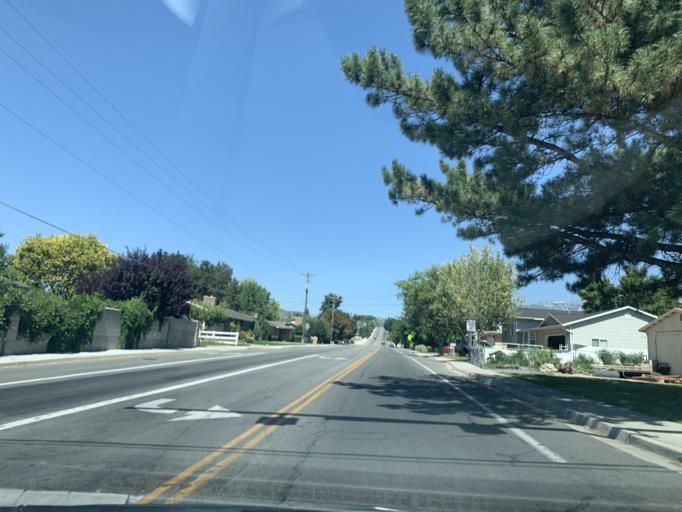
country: US
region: Utah
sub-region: Utah County
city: Lehi
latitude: 40.3990
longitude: -111.8302
